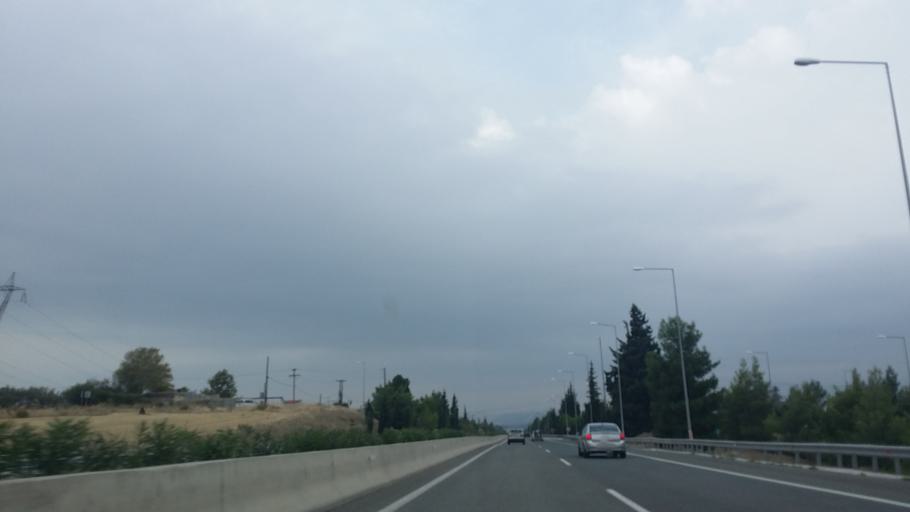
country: GR
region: Central Greece
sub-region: Nomos Voiotias
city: Schimatari
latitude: 38.3557
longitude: 23.5689
